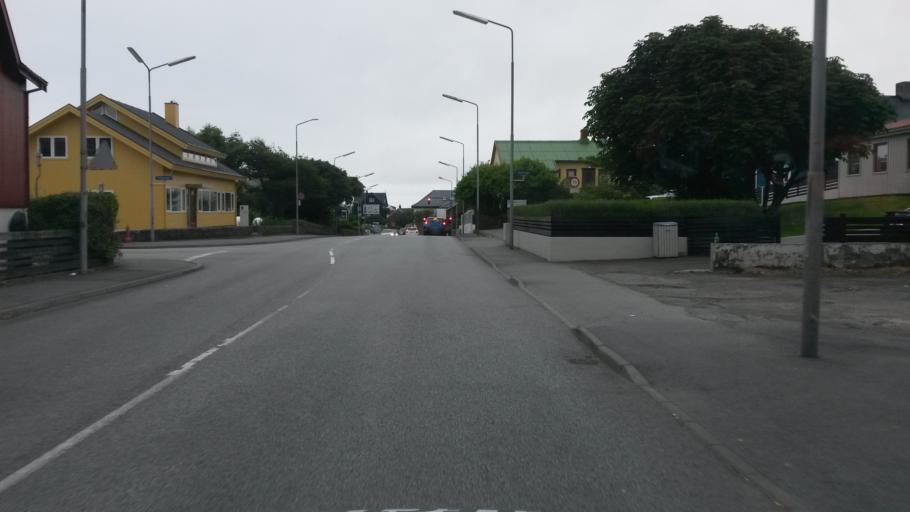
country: FO
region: Streymoy
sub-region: Torshavn
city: Torshavn
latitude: 62.0130
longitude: -6.7719
